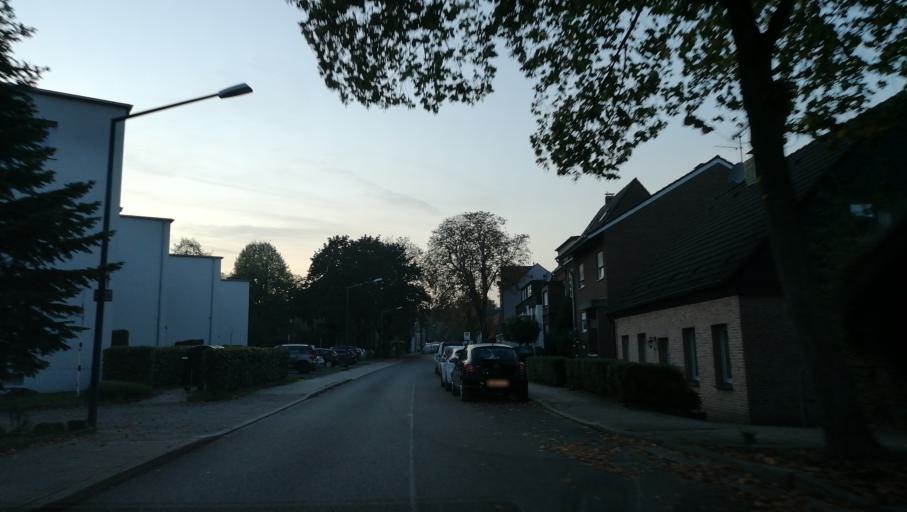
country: DE
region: North Rhine-Westphalia
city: Herten
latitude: 51.5898
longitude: 7.1466
